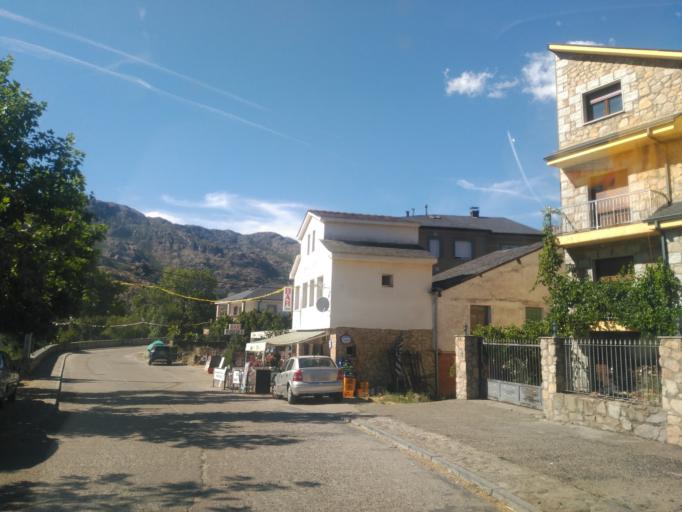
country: ES
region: Castille and Leon
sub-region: Provincia de Zamora
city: Cobreros
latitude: 42.1213
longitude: -6.7477
